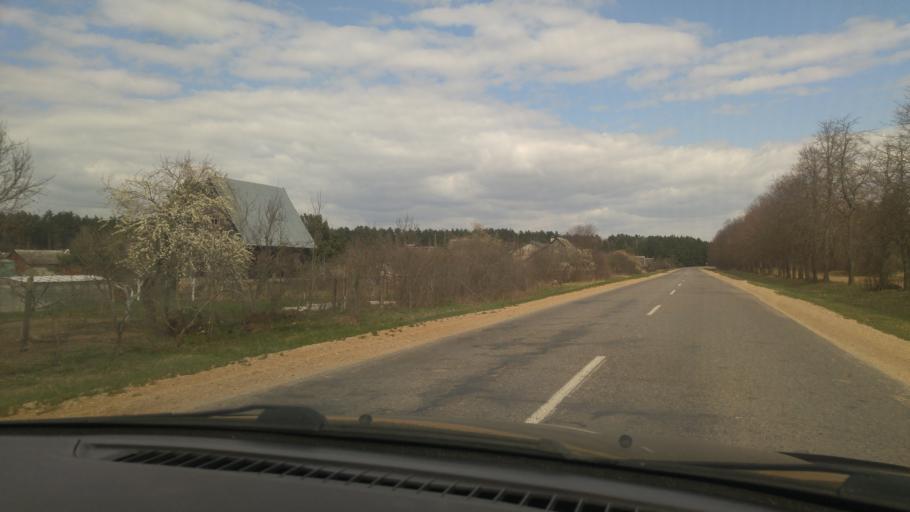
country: BY
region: Minsk
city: Rudzyensk
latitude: 53.6573
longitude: 27.8310
